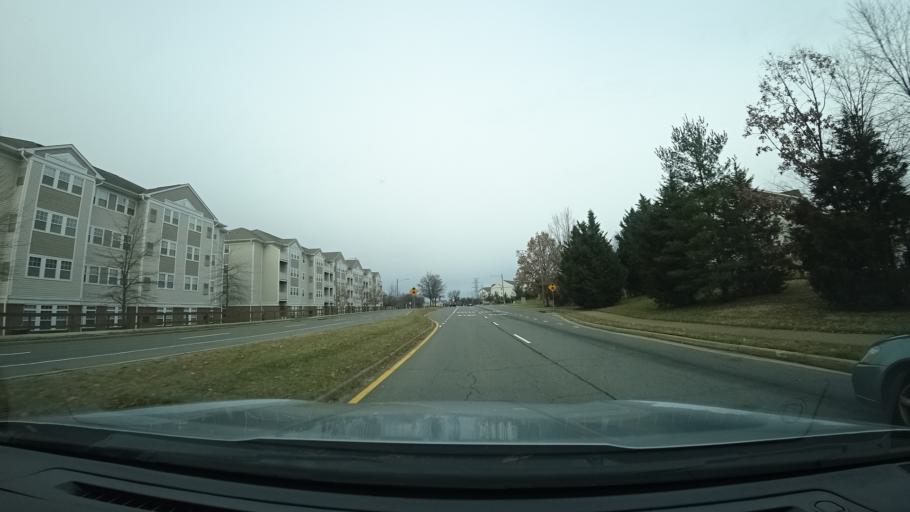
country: US
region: Virginia
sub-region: Fairfax County
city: Floris
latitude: 38.9460
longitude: -77.4083
